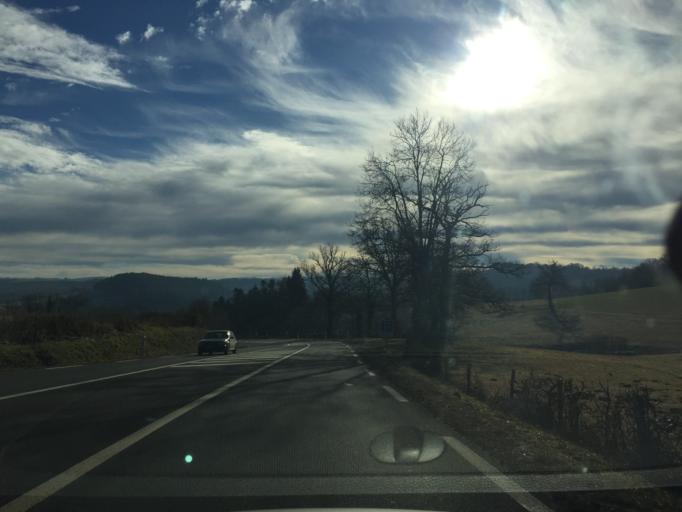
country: FR
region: Auvergne
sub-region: Departement du Puy-de-Dome
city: Gelles
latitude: 45.8605
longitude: 2.6418
